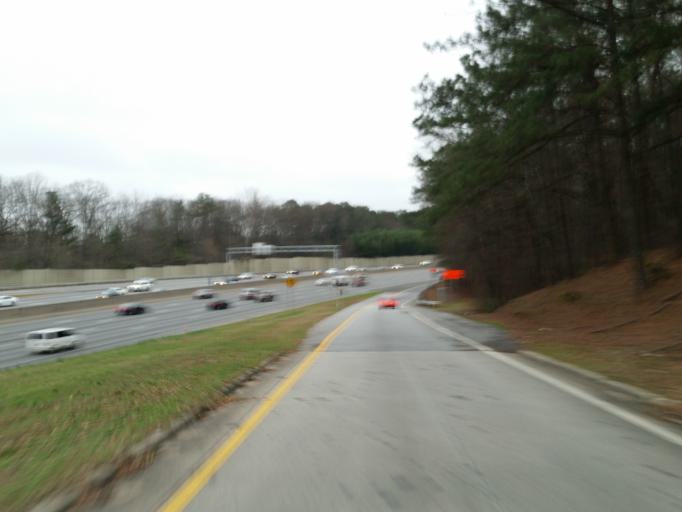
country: US
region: Georgia
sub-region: Fulton County
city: Sandy Springs
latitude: 33.9154
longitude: -84.4057
